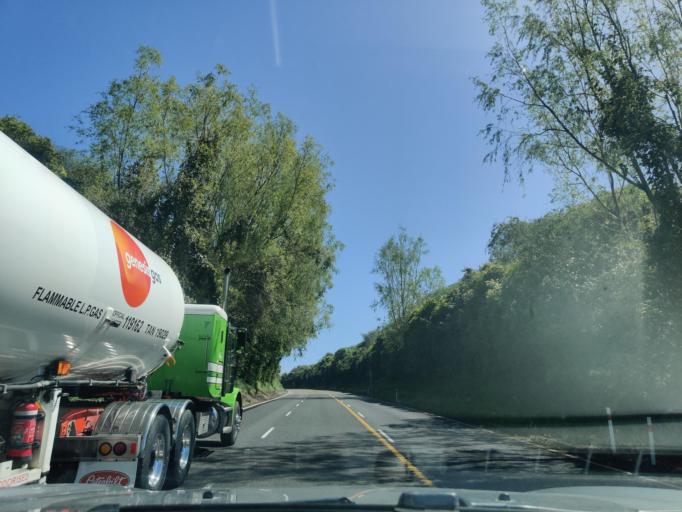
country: NZ
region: Manawatu-Wanganui
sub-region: Wanganui District
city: Wanganui
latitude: -39.8217
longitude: 174.8373
